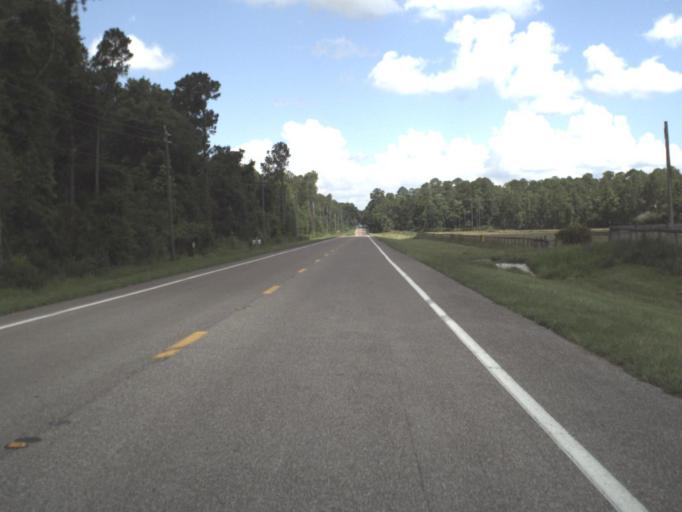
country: US
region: Florida
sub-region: Putnam County
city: East Palatka
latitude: 29.5893
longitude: -81.5656
